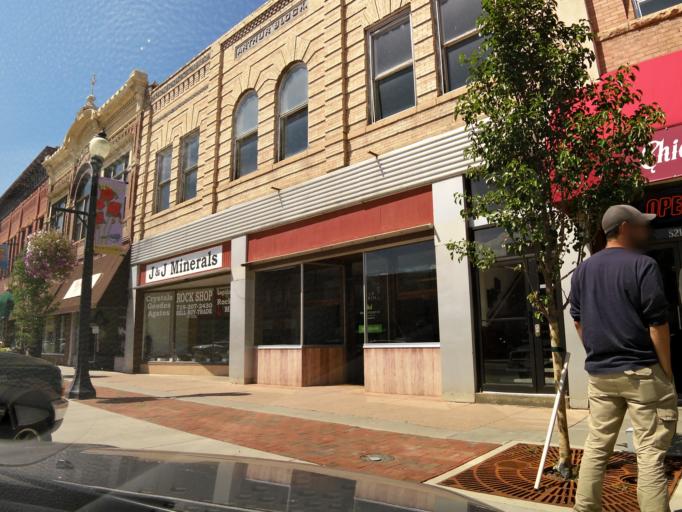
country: US
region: Colorado
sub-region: Fremont County
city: Canon City
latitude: 38.4410
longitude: -105.2399
